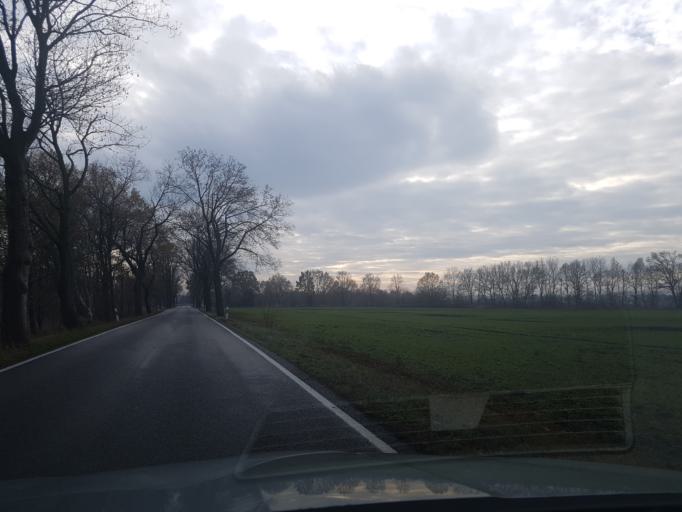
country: DE
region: Brandenburg
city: Plessa
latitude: 51.4376
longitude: 13.6238
